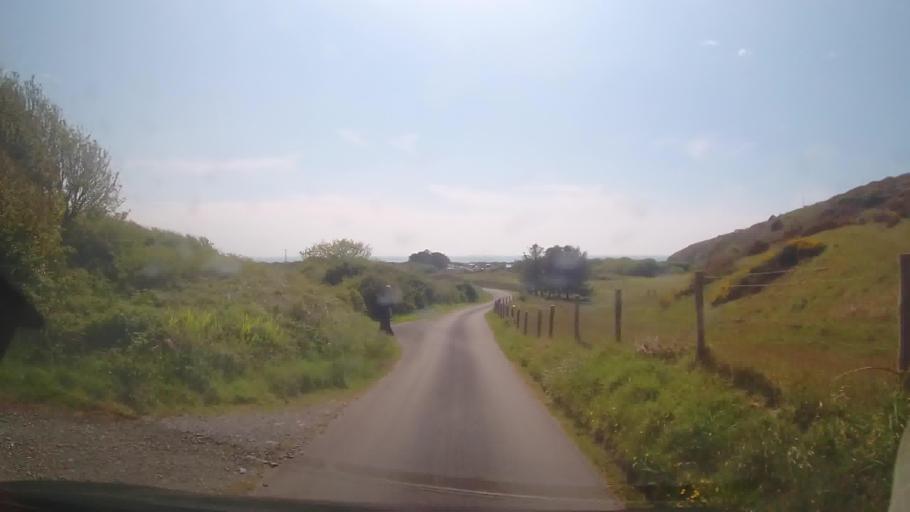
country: GB
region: Wales
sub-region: Gwynedd
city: Criccieth
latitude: 52.9175
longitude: -4.1890
